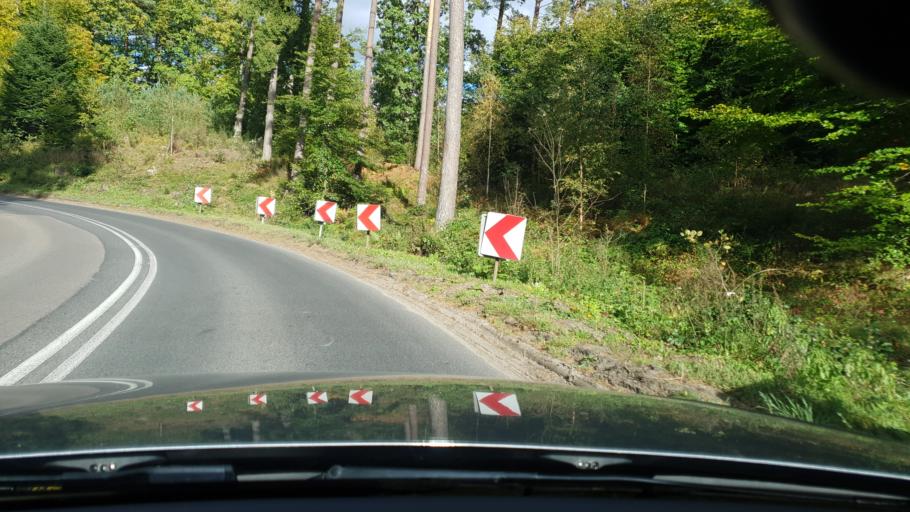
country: PL
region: Pomeranian Voivodeship
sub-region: Powiat wejherowski
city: Koleczkowo
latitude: 54.4971
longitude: 18.3612
